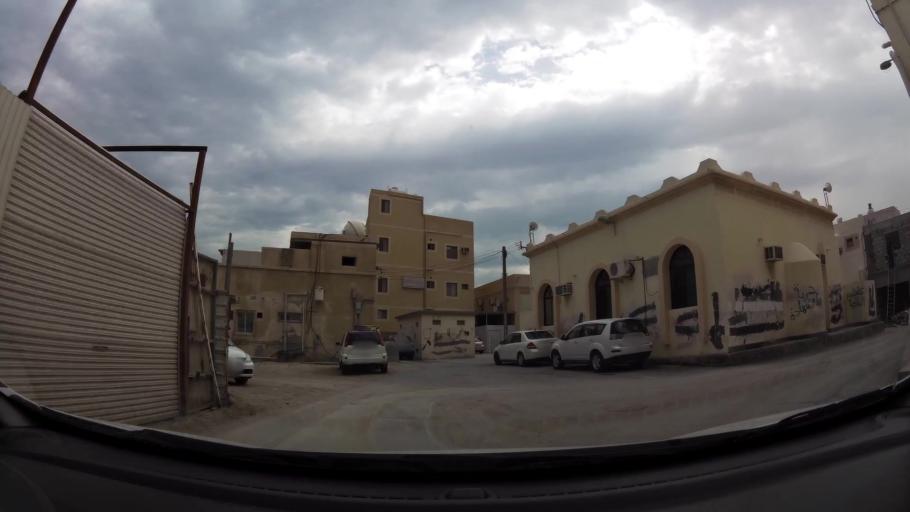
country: BH
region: Manama
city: Manama
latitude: 26.1852
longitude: 50.5832
